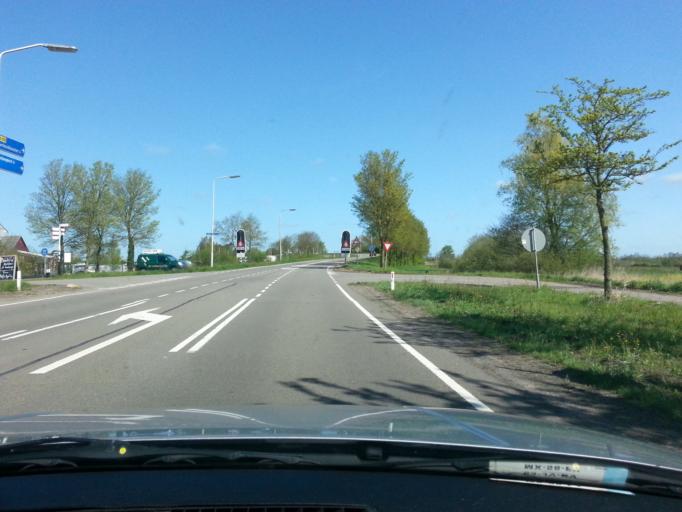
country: NL
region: Friesland
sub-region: Gemeente Achtkarspelen
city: Augustinusga
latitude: 53.2232
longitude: 6.1748
